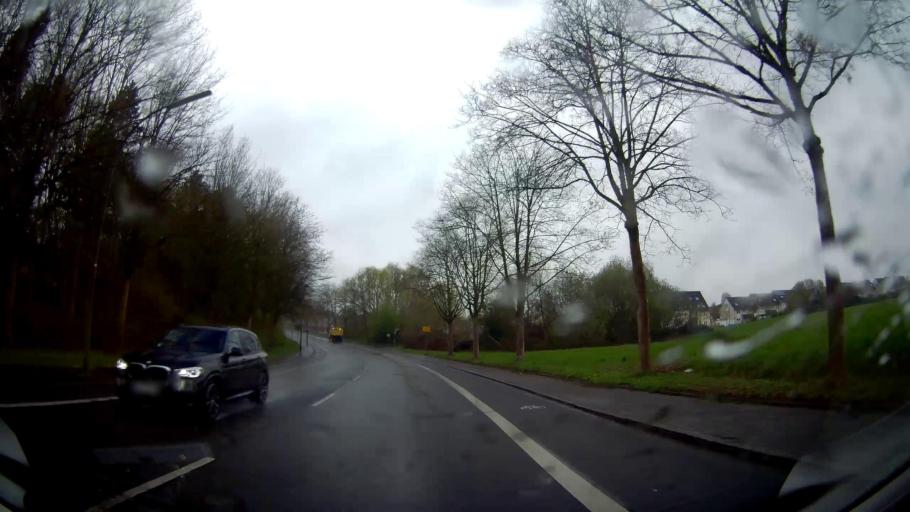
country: DE
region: North Rhine-Westphalia
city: Witten
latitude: 51.5037
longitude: 7.3458
